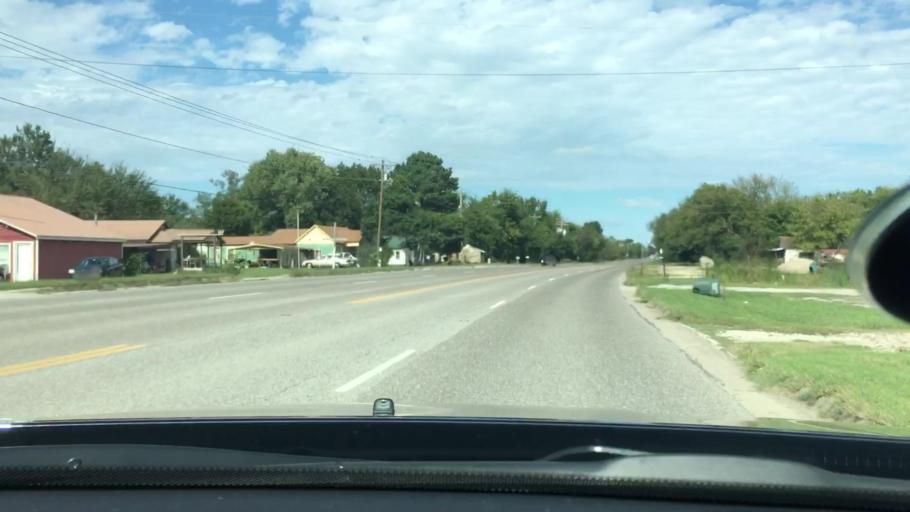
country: US
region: Oklahoma
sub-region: Murray County
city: Davis
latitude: 34.4864
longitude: -97.1302
